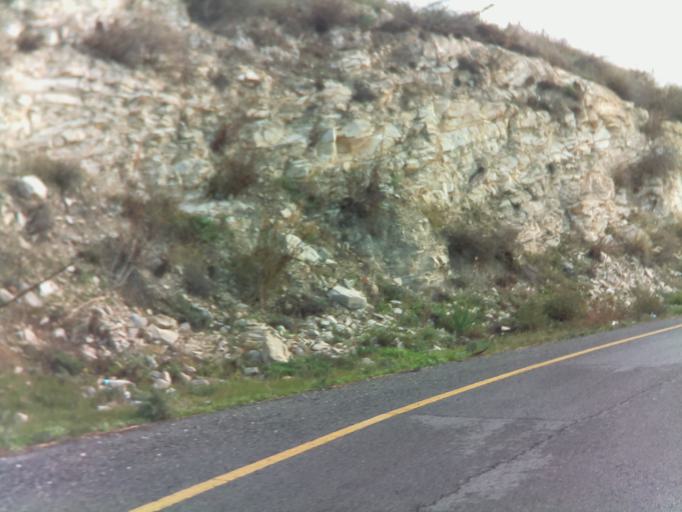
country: CY
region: Pafos
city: Pegeia
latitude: 34.8863
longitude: 32.3771
